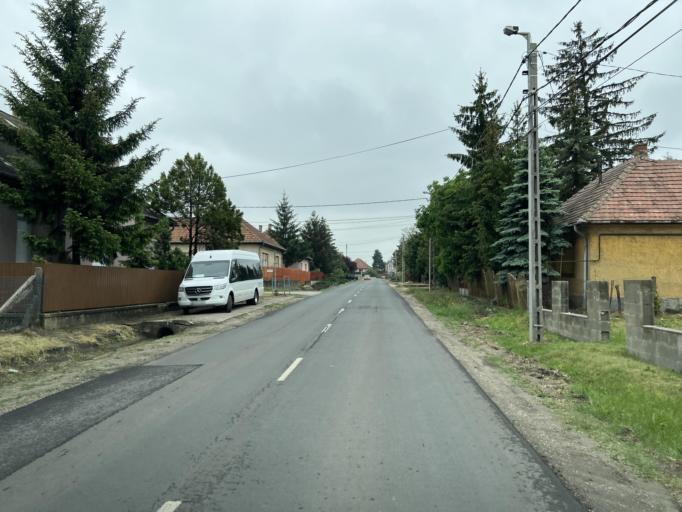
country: HU
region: Pest
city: Tura
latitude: 47.6045
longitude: 19.5938
